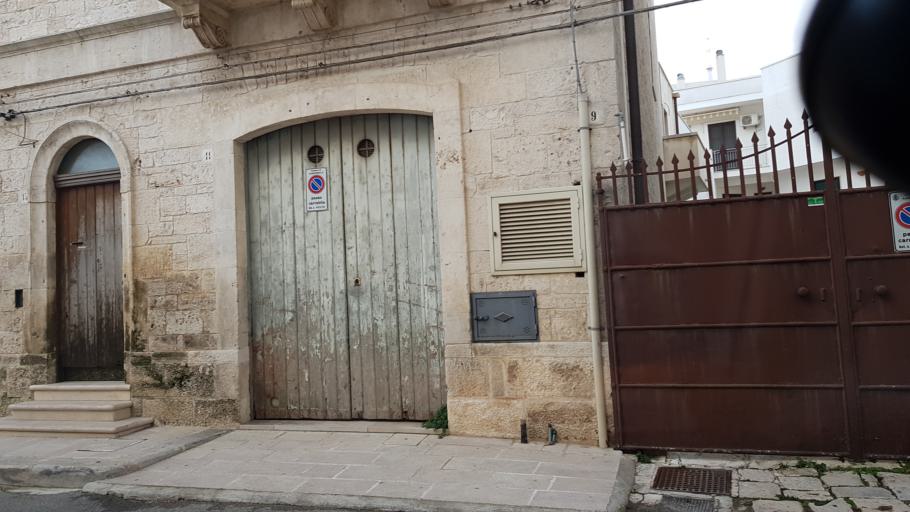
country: IT
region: Apulia
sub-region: Provincia di Bari
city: Alberobello
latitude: 40.7852
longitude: 17.2406
